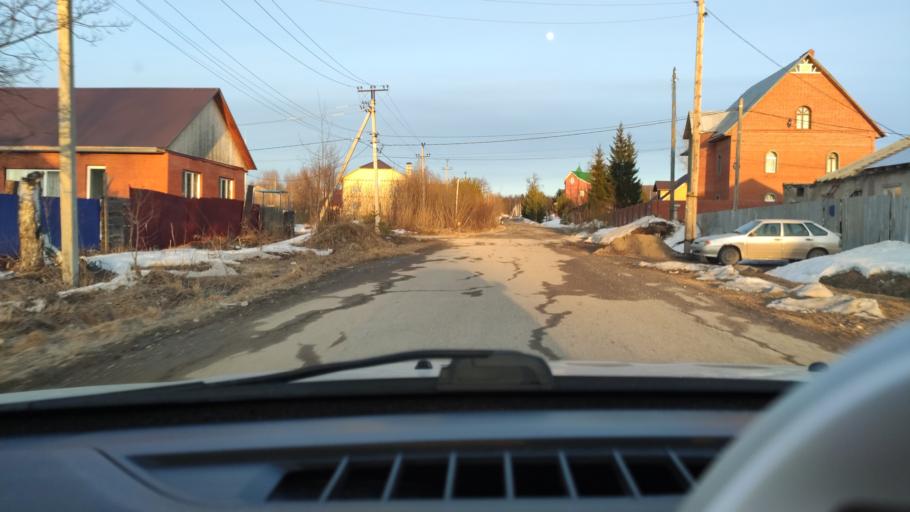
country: RU
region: Perm
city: Polazna
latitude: 58.1164
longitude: 56.4077
